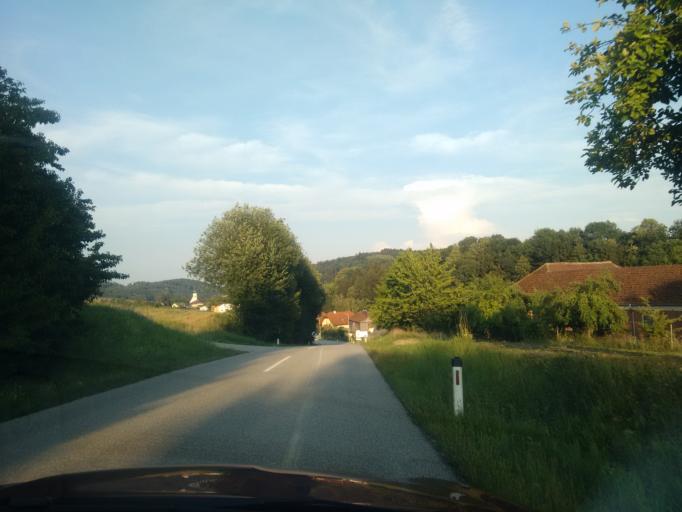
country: AT
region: Upper Austria
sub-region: Wels-Land
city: Offenhausen
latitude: 48.1563
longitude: 13.8240
